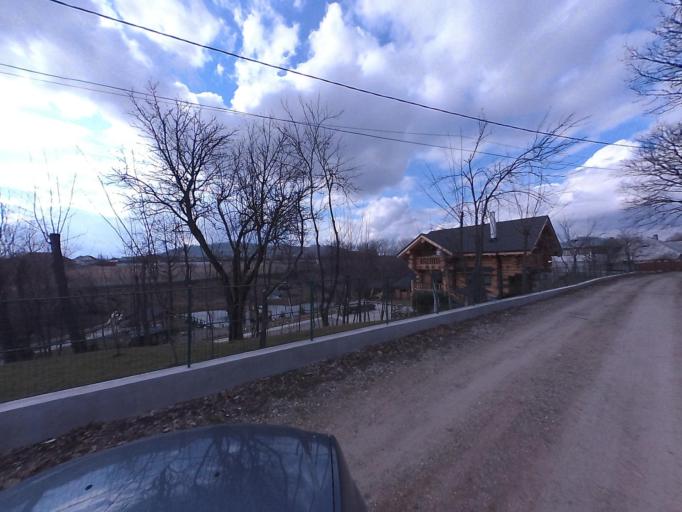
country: RO
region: Neamt
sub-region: Oras Targu Neamt
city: Targu Neamt
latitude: 47.2162
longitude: 26.3813
